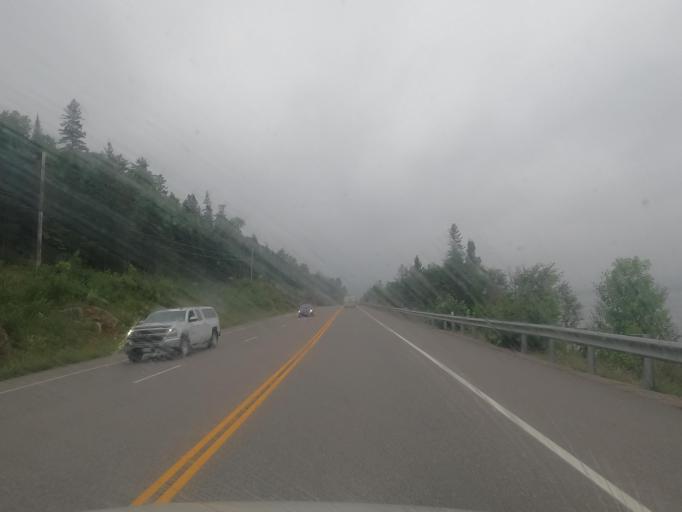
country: CA
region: Ontario
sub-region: Algoma
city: Sault Ste. Marie
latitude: 46.8306
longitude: -84.3934
